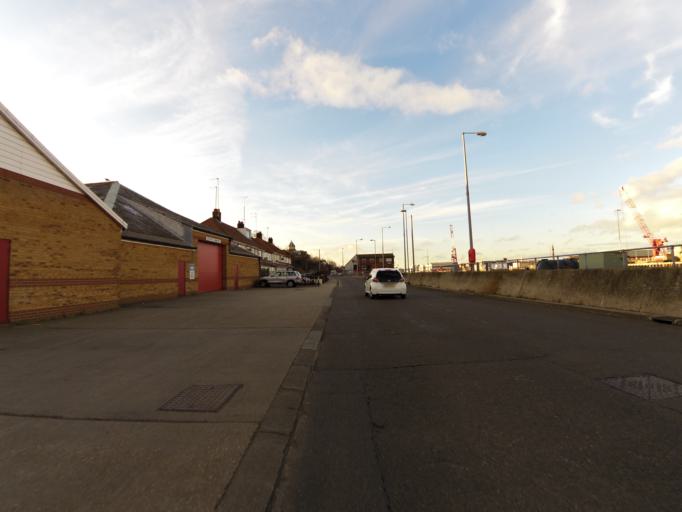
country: GB
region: England
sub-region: Norfolk
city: Gorleston-on-Sea
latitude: 52.5818
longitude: 1.7303
